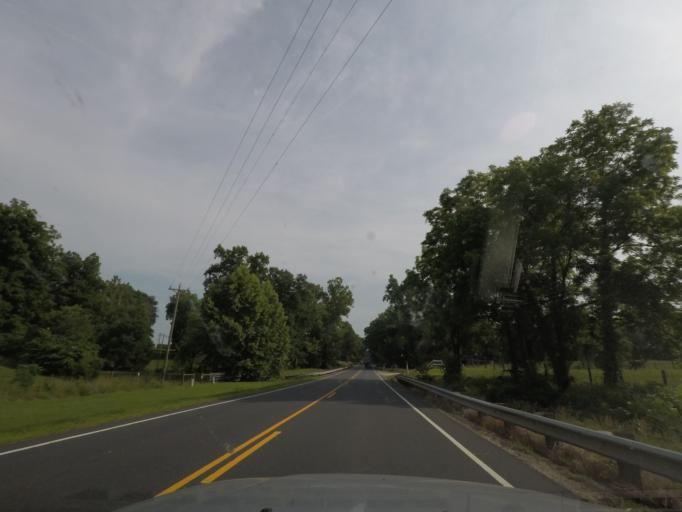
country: US
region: Virginia
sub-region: Prince Edward County
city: Hampden Sydney
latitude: 37.2197
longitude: -78.4420
